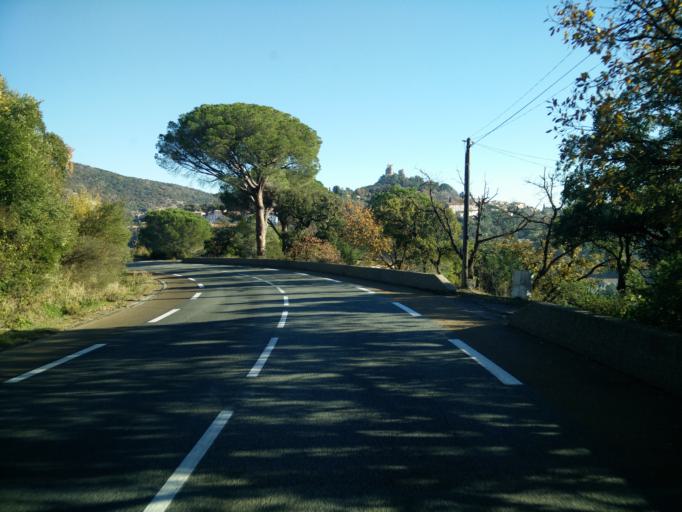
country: FR
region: Provence-Alpes-Cote d'Azur
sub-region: Departement du Var
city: Grimaud
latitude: 43.2727
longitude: 6.5118
